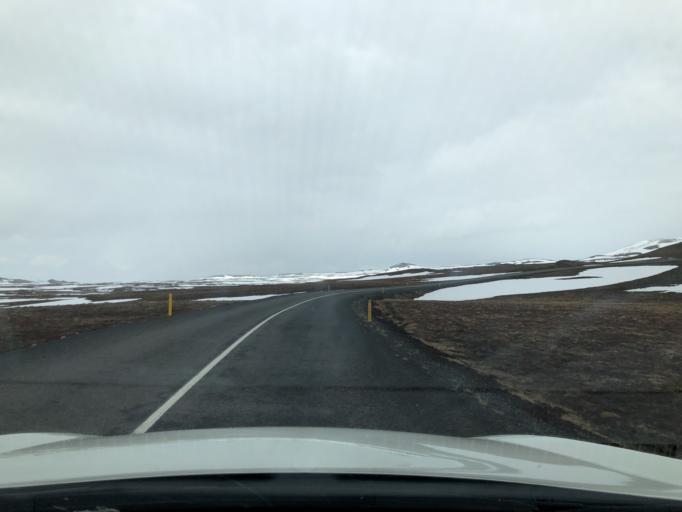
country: IS
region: Northeast
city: Laugar
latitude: 65.7155
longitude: -16.7620
